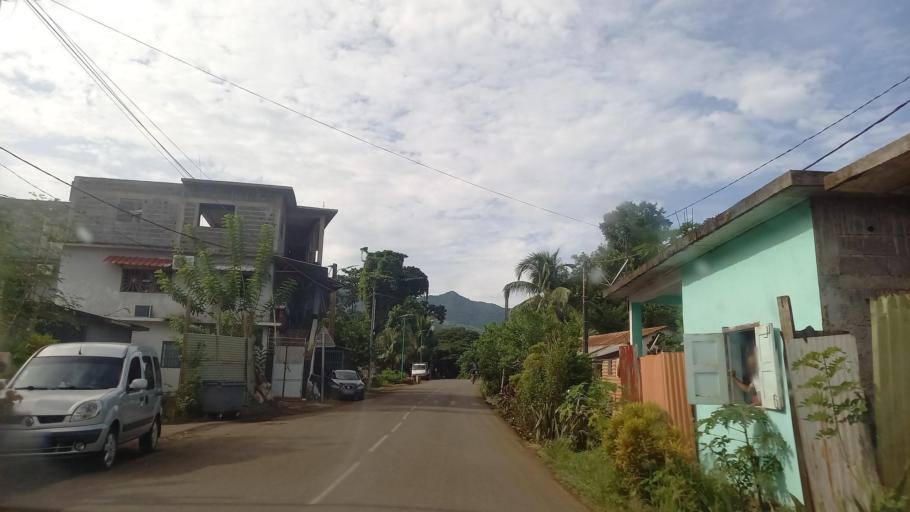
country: YT
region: Chirongui
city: Chirongui
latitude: -12.9200
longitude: 45.1589
